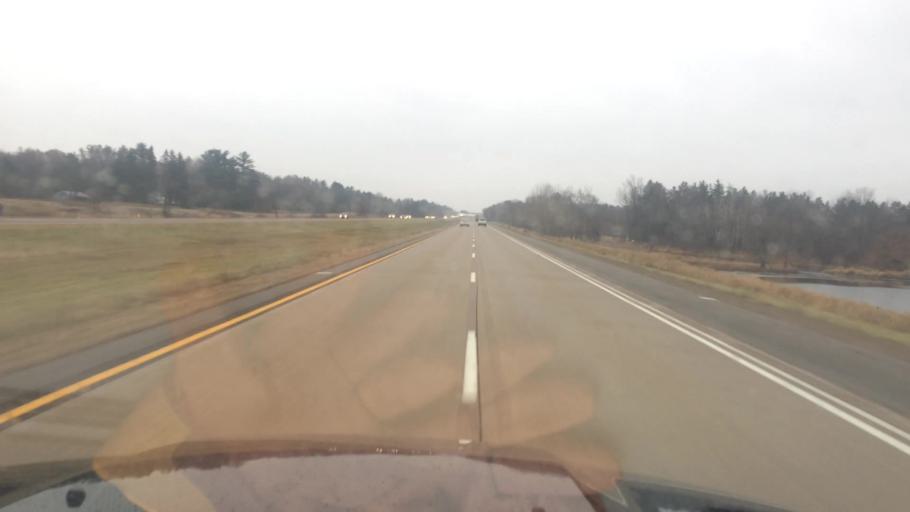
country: US
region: Wisconsin
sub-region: Portage County
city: Stevens Point
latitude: 44.6130
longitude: -89.6244
